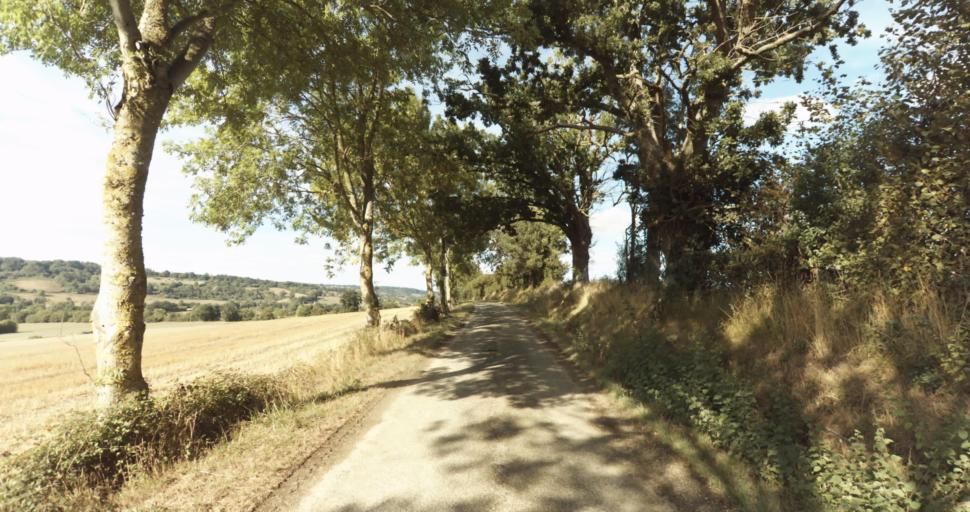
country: FR
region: Lower Normandy
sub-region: Departement du Calvados
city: Livarot
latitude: 48.9339
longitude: 0.1210
